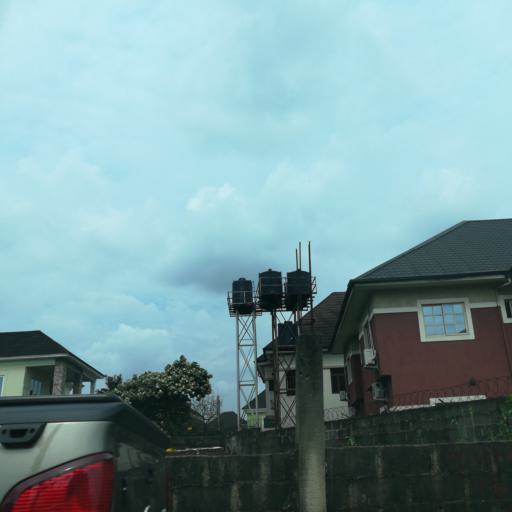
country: NG
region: Rivers
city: Port Harcourt
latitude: 4.8257
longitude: 6.9851
